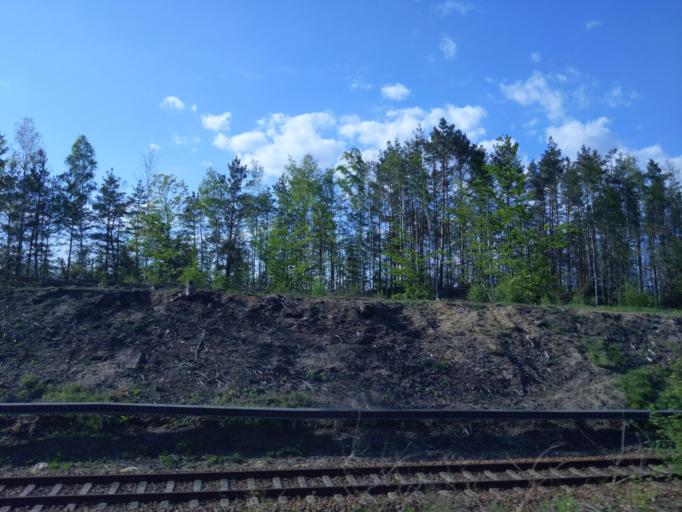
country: DE
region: Saxony
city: Albertstadt
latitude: 51.1279
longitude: 13.8056
